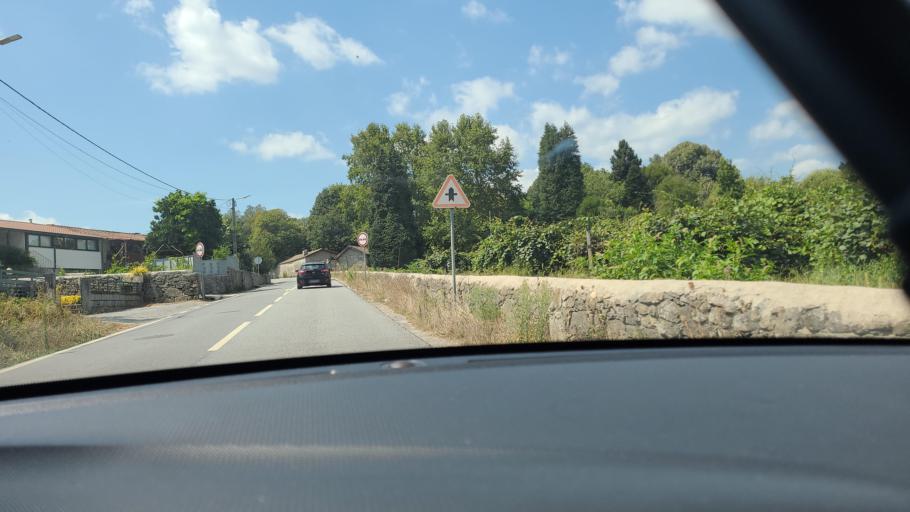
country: PT
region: Braga
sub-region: Amares
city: Amares
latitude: 41.6236
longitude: -8.3388
